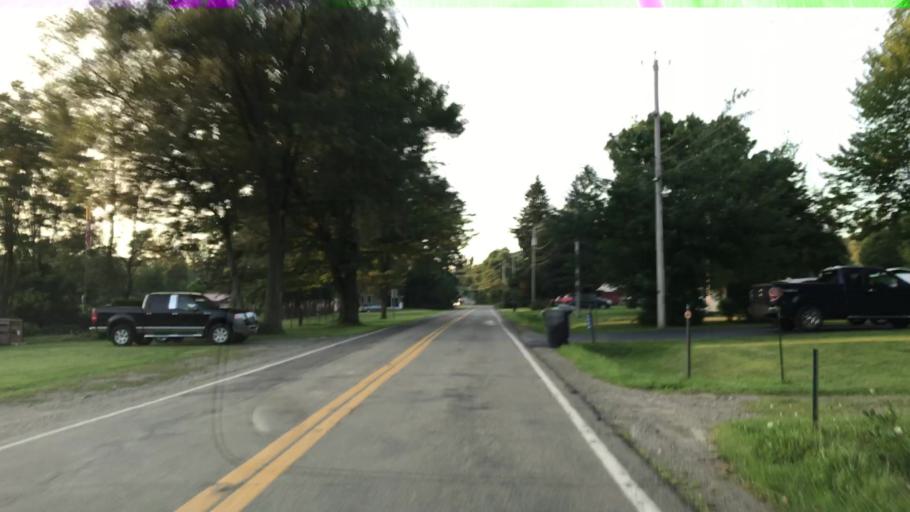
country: US
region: New York
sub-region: Chautauqua County
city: Mayville
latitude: 42.2633
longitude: -79.4706
